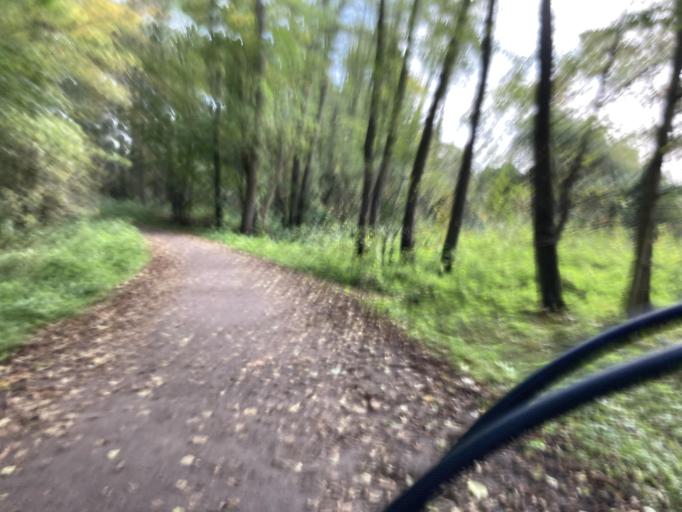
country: DE
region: North Rhine-Westphalia
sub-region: Regierungsbezirk Munster
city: Muenster
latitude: 51.9845
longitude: 7.6915
